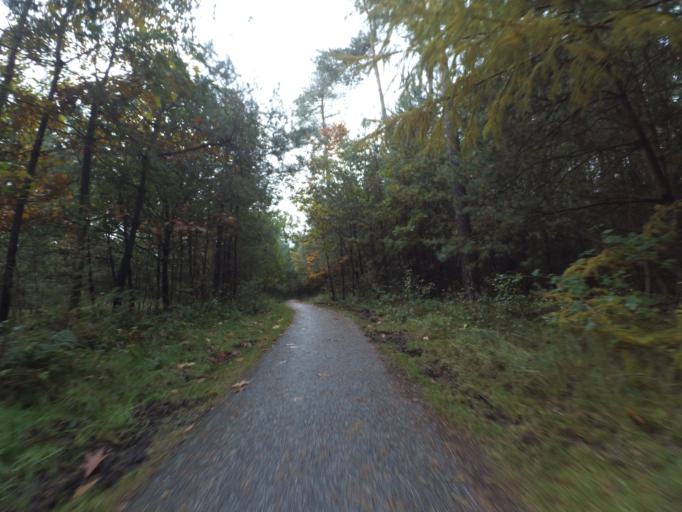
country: NL
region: Gelderland
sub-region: Gemeente Apeldoorn
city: Uddel
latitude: 52.3150
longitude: 5.7433
